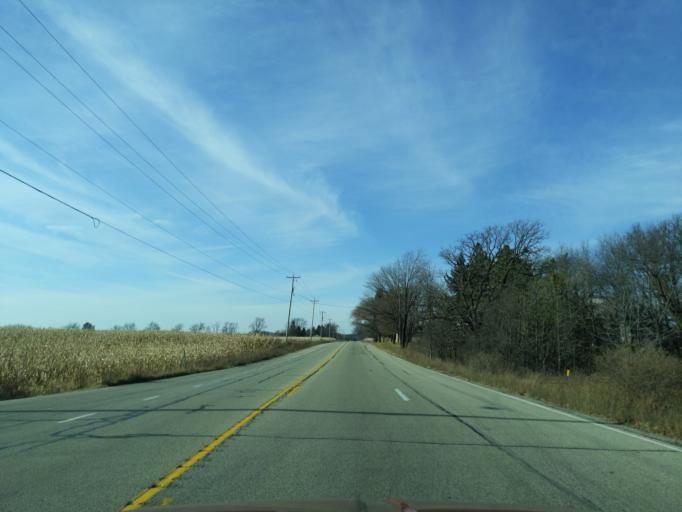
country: US
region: Wisconsin
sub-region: Jefferson County
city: Palmyra
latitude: 42.7957
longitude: -88.6262
